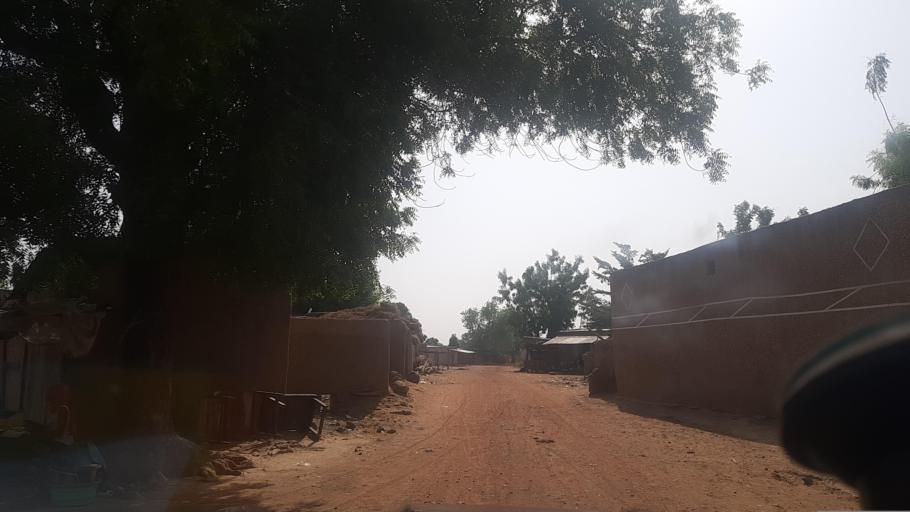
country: ML
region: Segou
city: Baroueli
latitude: 13.1662
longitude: -6.5197
